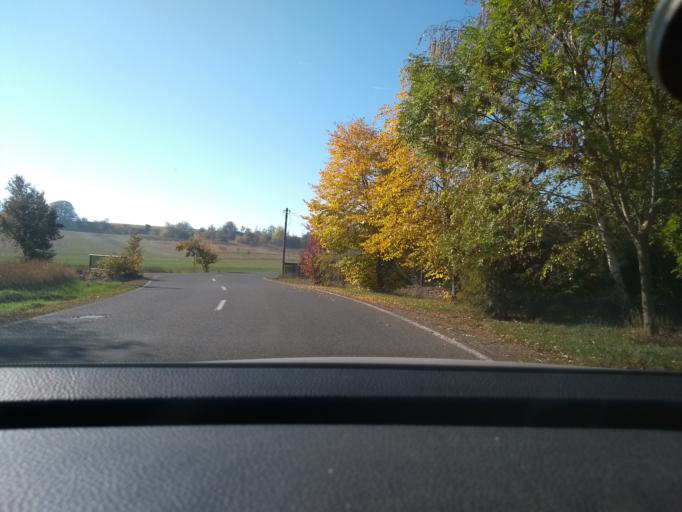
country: DE
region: Saxony-Anhalt
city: Farnstadt
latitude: 51.4545
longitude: 11.5947
